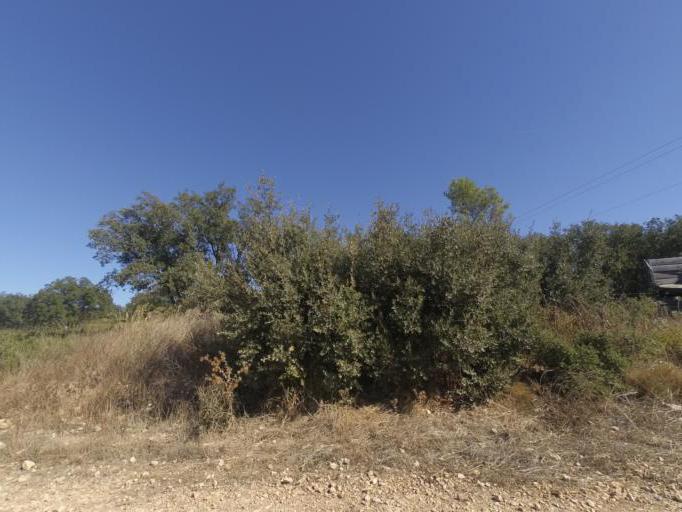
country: FR
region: Languedoc-Roussillon
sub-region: Departement du Gard
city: Nages-et-Solorgues
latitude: 43.7656
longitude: 4.2394
